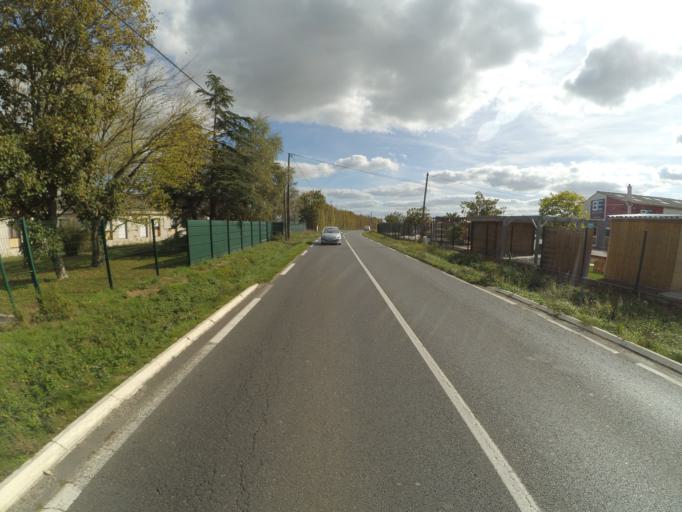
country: FR
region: Pays de la Loire
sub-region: Departement de la Loire-Atlantique
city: Carquefou
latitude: 47.2891
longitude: -1.4656
